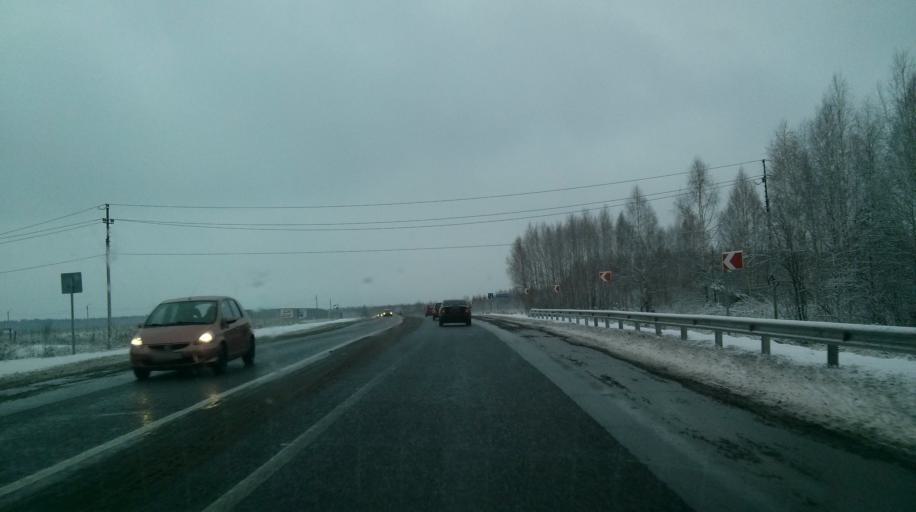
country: RU
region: Nizjnij Novgorod
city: Bogorodsk
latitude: 56.1254
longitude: 43.5989
